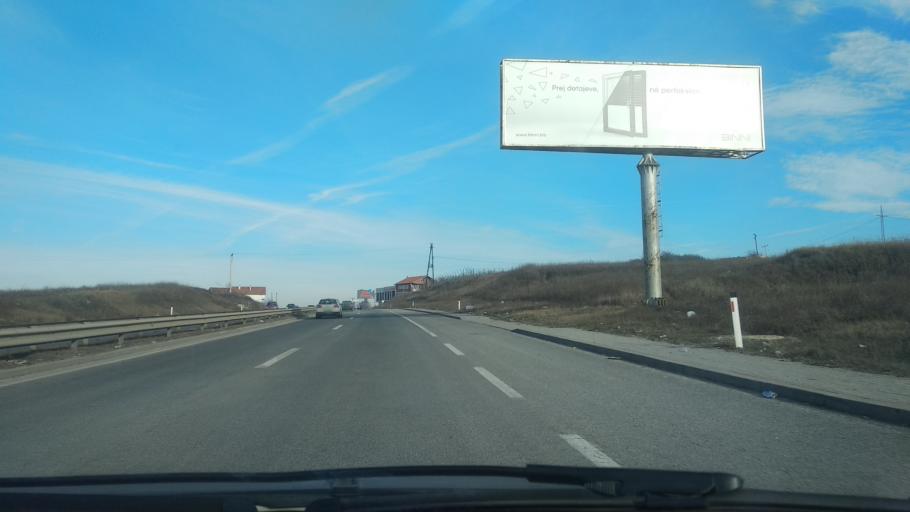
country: XK
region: Pristina
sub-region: Kosovo Polje
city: Kosovo Polje
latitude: 42.6884
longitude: 21.1187
